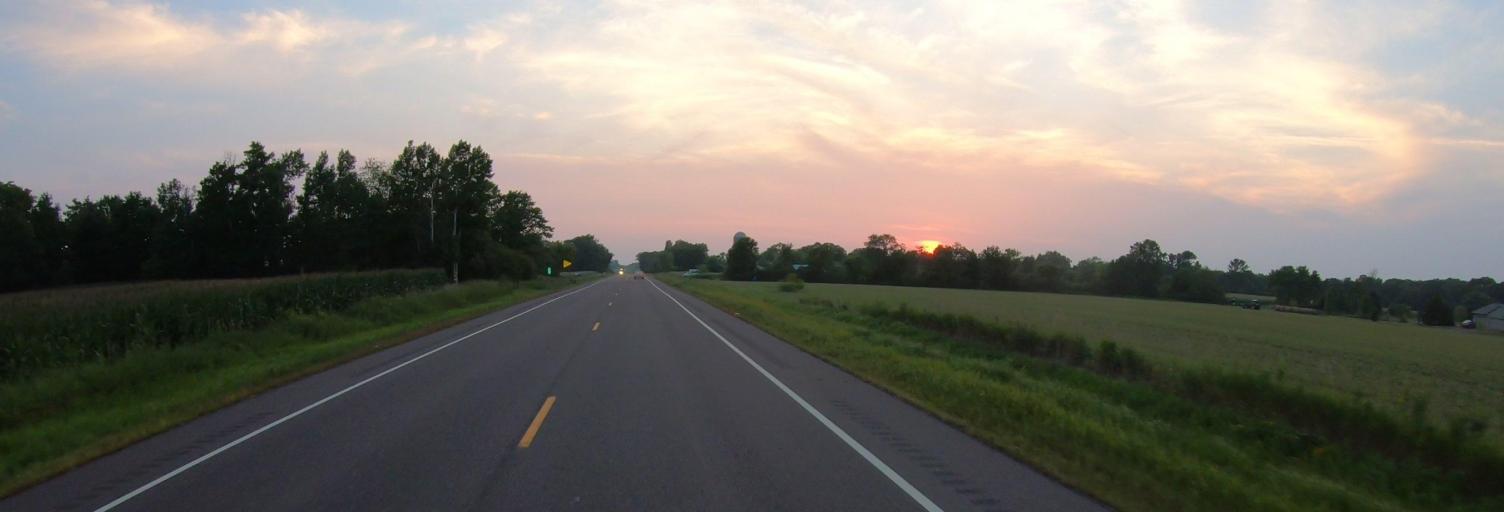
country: US
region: Minnesota
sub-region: Pine County
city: Rock Creek
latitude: 45.7735
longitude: -92.9114
